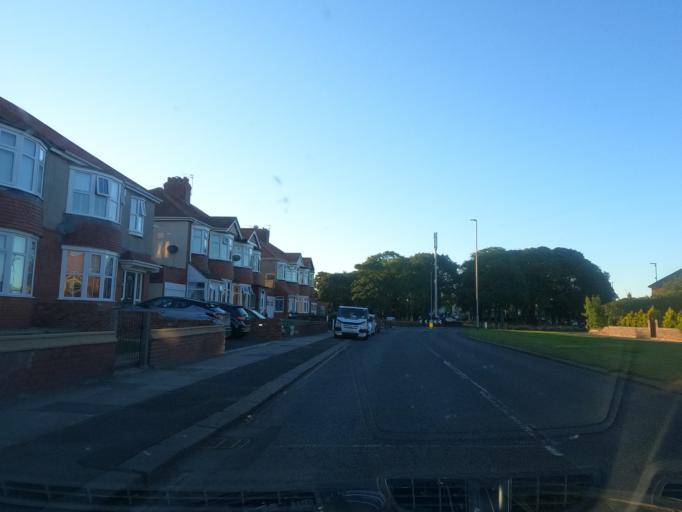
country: GB
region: England
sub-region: Northumberland
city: Blyth
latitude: 55.1220
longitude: -1.5151
